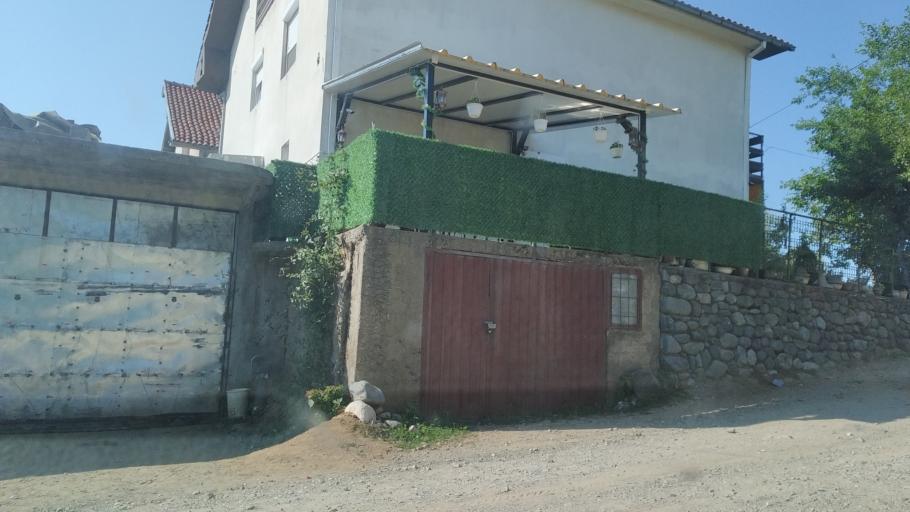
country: MK
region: Bogdanci
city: Bogdanci
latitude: 41.2030
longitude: 22.5701
